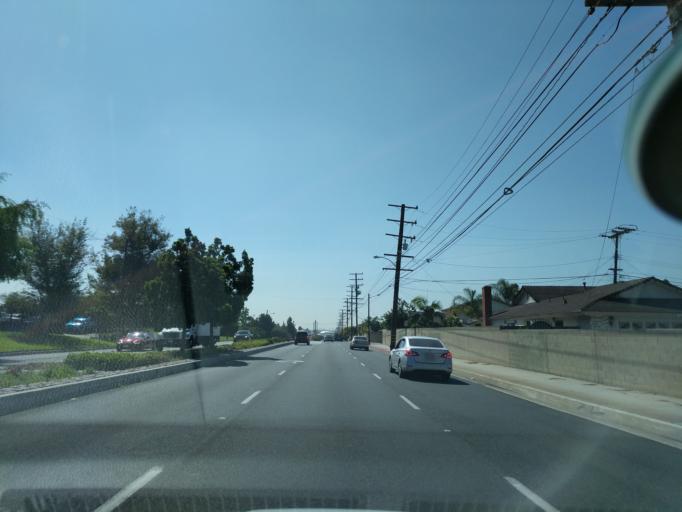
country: US
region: California
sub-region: Los Angeles County
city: Compton
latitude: 33.8530
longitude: -118.2345
